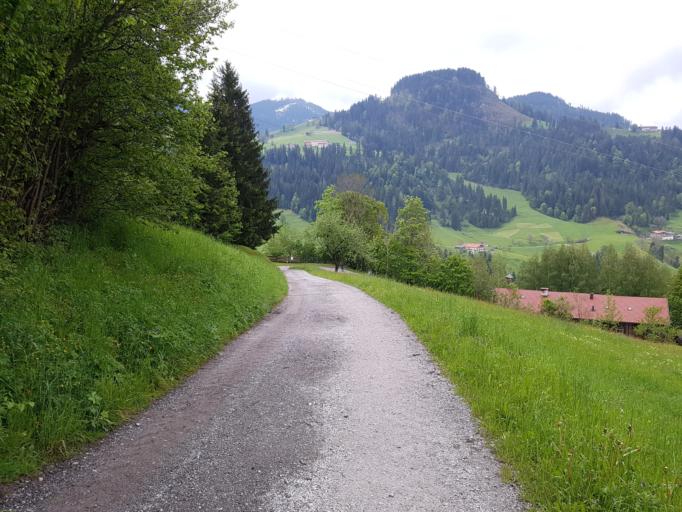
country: AT
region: Tyrol
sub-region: Politischer Bezirk Kufstein
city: Soll
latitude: 47.4938
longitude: 12.2062
